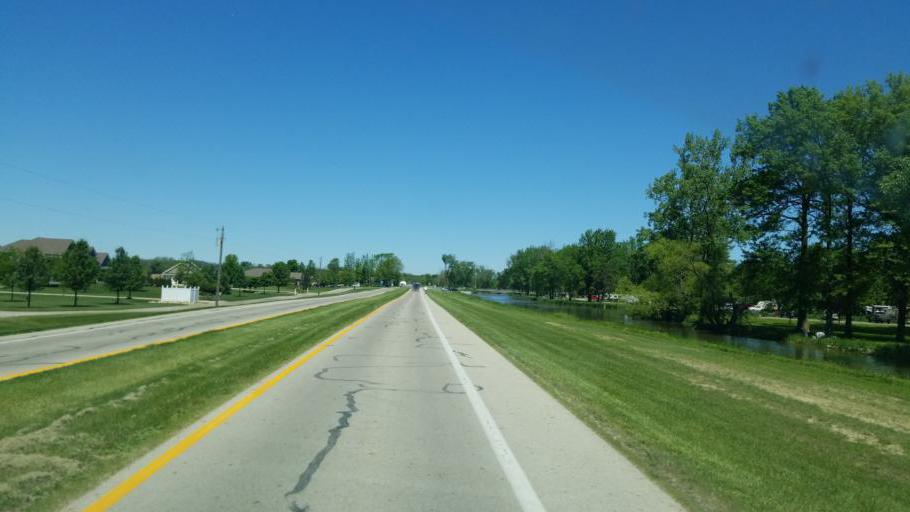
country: US
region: Ohio
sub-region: Shelby County
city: Fort Loramie
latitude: 40.3535
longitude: -84.3547
